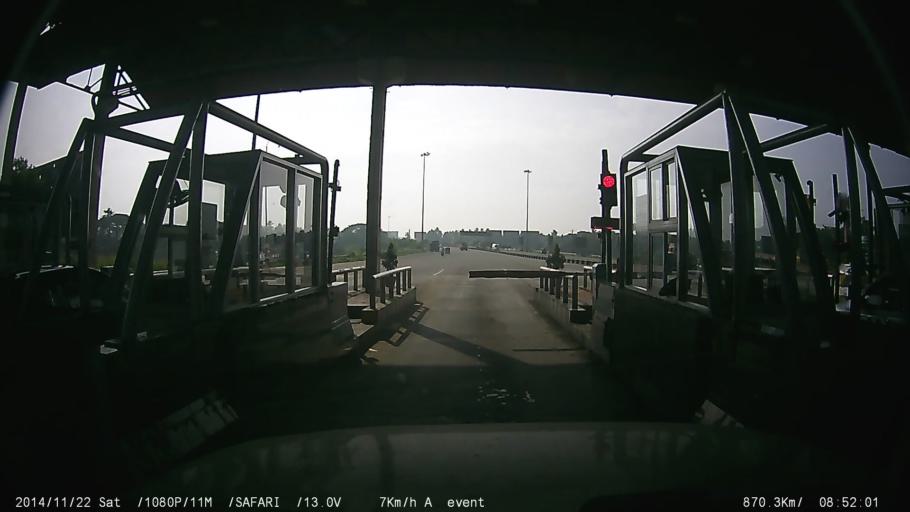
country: IN
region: Kerala
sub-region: Thrissur District
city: Trichur
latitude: 10.4430
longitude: 76.2602
